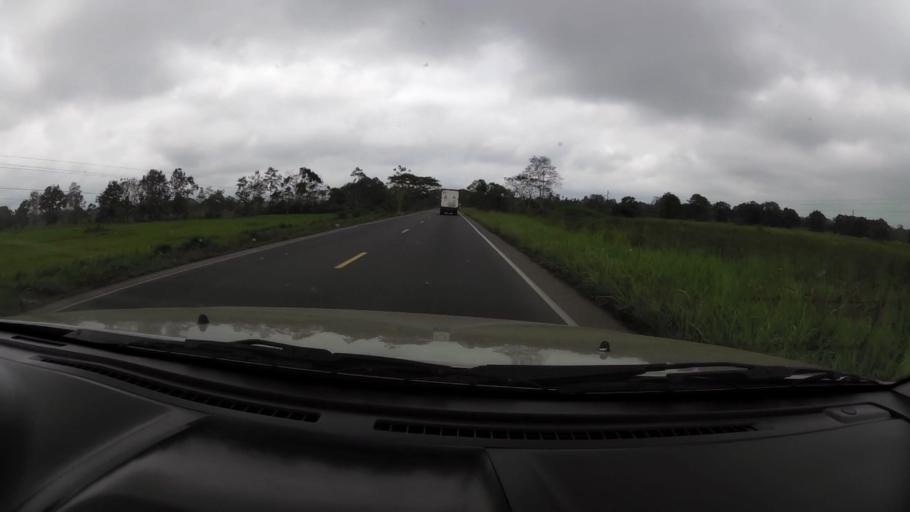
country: EC
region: Guayas
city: Balao
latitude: -2.8756
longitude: -79.7043
